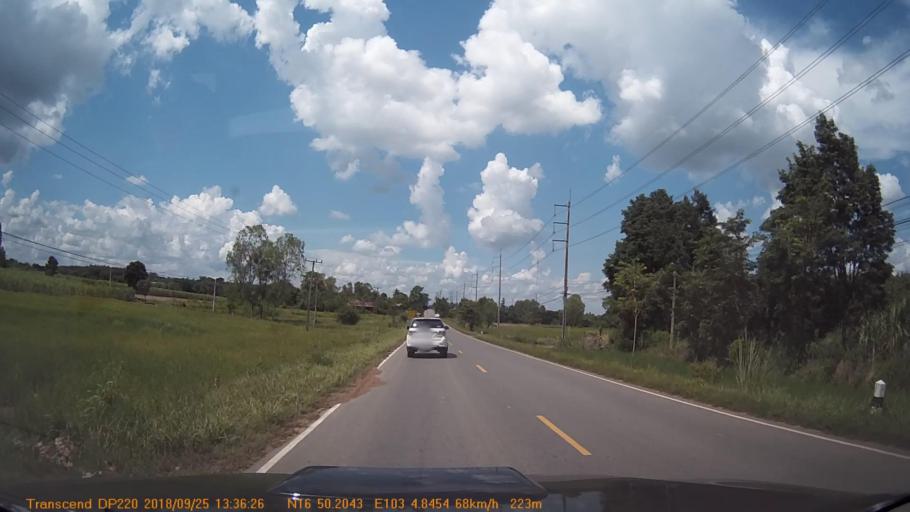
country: TH
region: Khon Kaen
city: Kranuan
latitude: 16.8369
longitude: 103.0808
